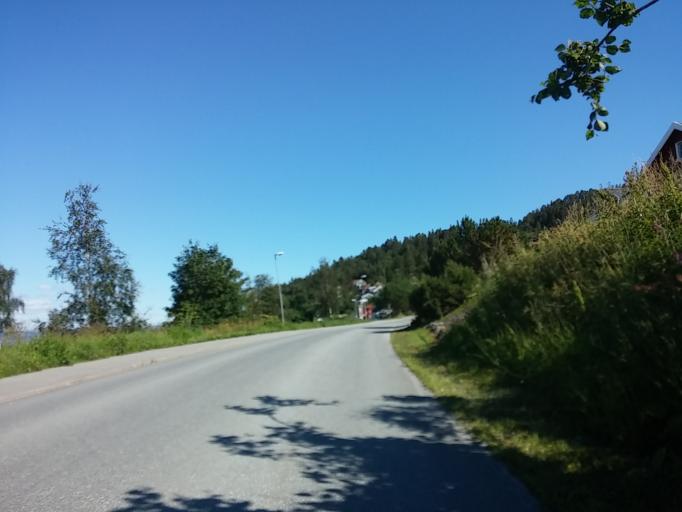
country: NO
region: Sor-Trondelag
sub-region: Malvik
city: Hommelvik
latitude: 63.4324
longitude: 10.7430
